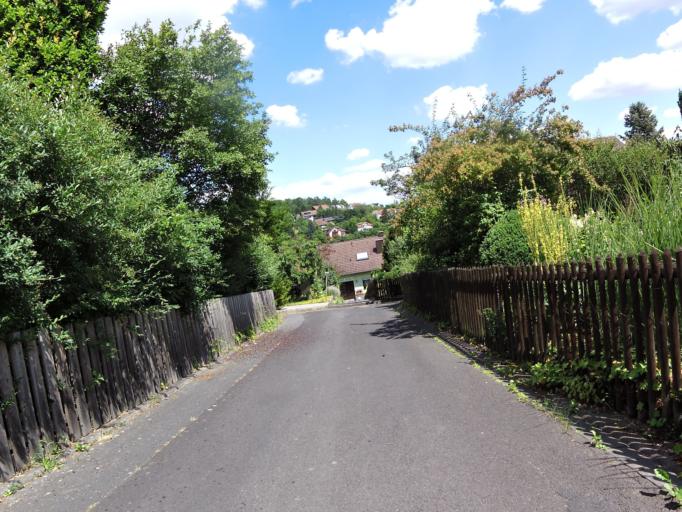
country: DE
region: Bavaria
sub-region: Regierungsbezirk Unterfranken
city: Gadheim
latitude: 49.8297
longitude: 9.9166
